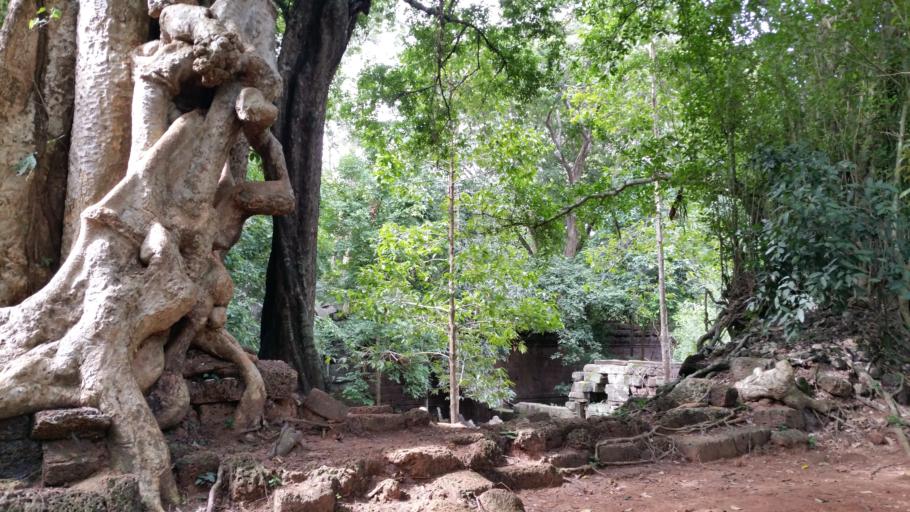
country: KH
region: Siem Reap
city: Siem Reap
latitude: 13.4443
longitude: 103.8552
